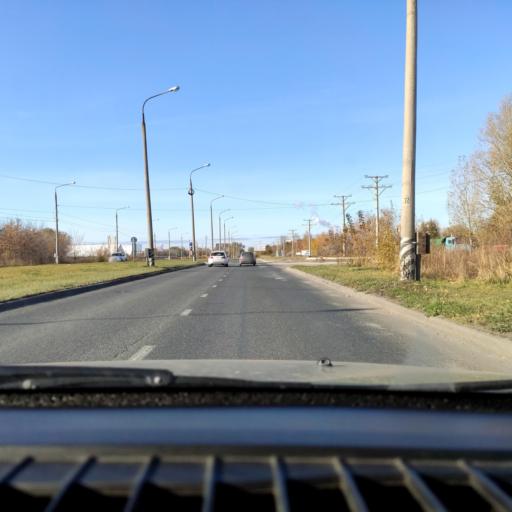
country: RU
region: Samara
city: Tol'yatti
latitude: 53.5580
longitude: 49.3270
